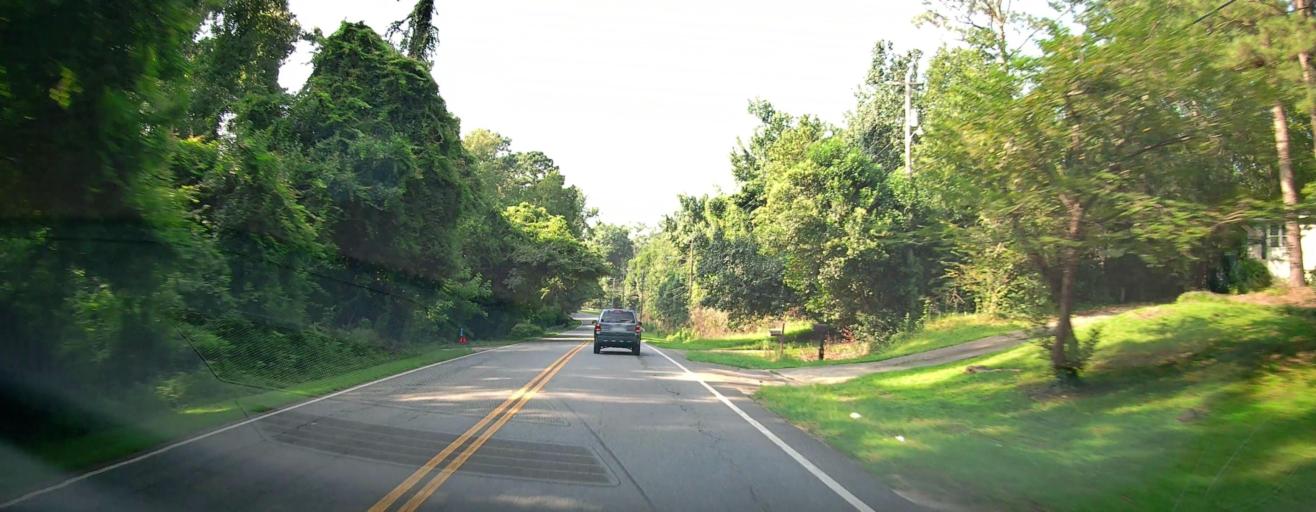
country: US
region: Georgia
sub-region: Bibb County
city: Macon
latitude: 32.8627
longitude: -83.6614
